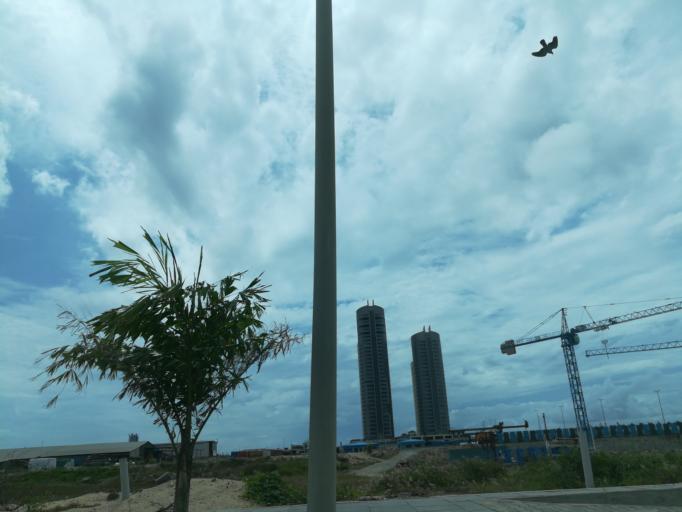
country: NG
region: Lagos
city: Lagos
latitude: 6.4116
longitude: 3.4064
